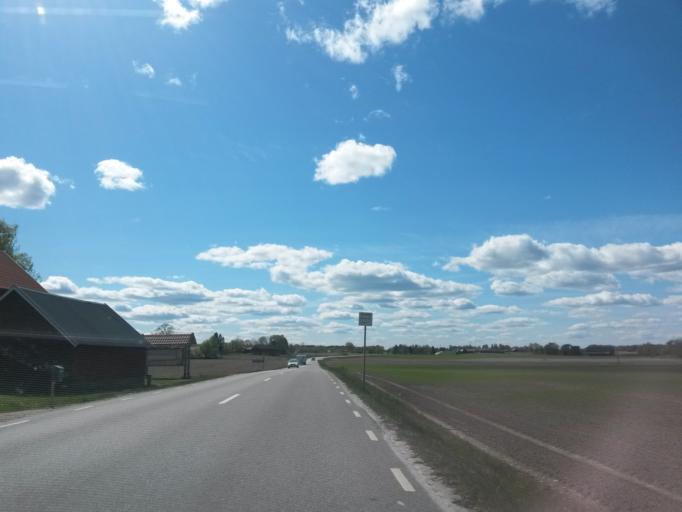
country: SE
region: Vaestra Goetaland
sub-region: Herrljunga Kommun
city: Herrljunga
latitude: 58.0742
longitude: 12.9986
